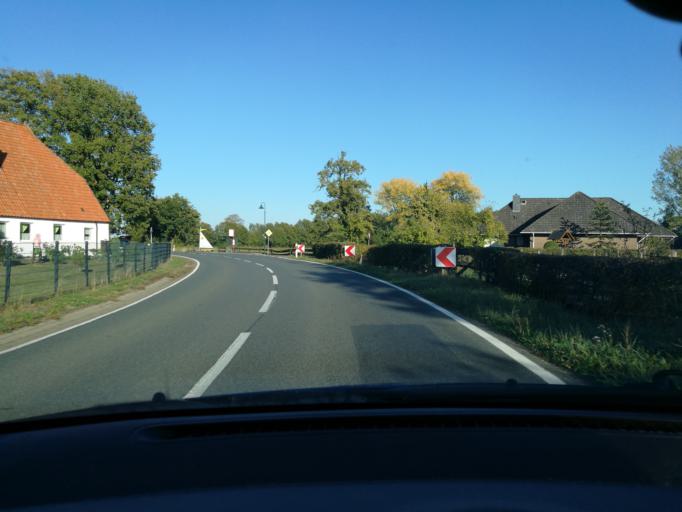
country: DE
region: Lower Saxony
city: Neetze
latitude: 53.3150
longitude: 10.6332
